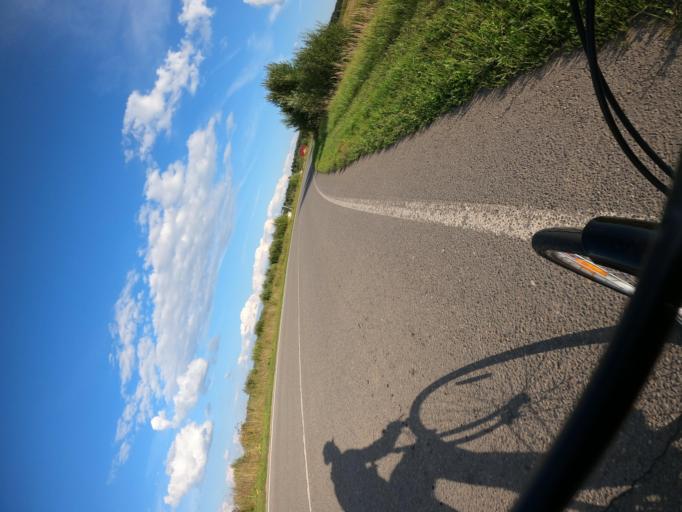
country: RU
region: Moskovskaya
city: Meshcherino
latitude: 55.1453
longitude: 38.4400
